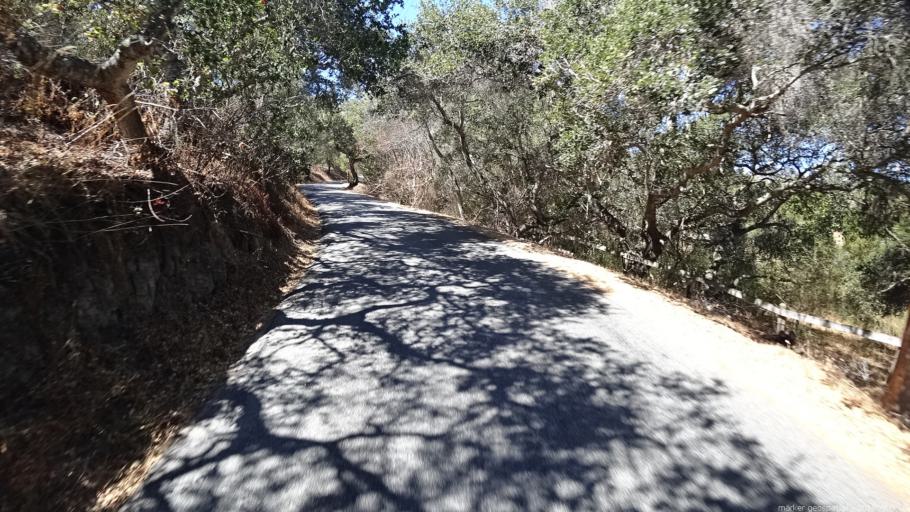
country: US
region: California
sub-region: Monterey County
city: Carmel Valley Village
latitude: 36.5514
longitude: -121.7382
